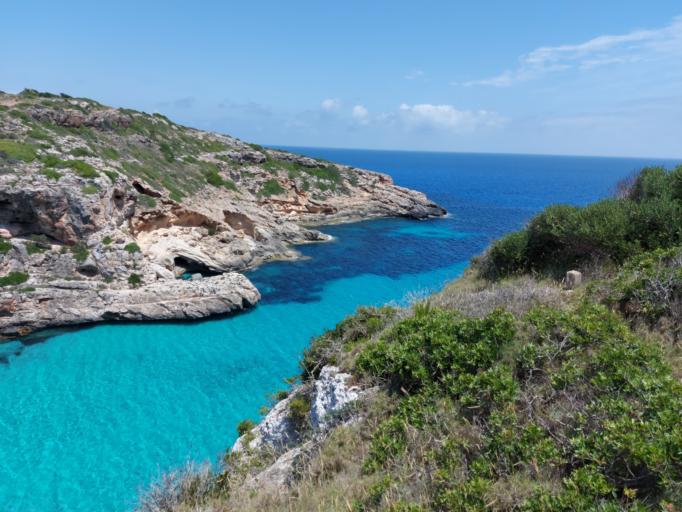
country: ES
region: Balearic Islands
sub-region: Illes Balears
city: Ses Salines
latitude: 39.2886
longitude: 3.0903
